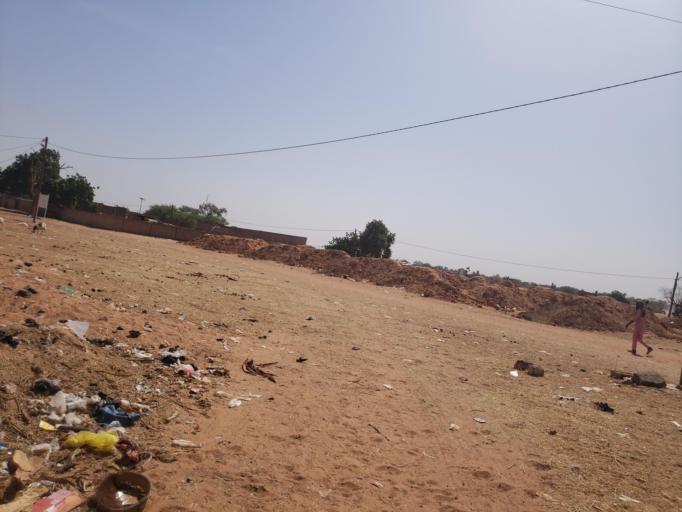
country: SN
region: Matam
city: Ranerou
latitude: 15.2981
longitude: -13.9639
